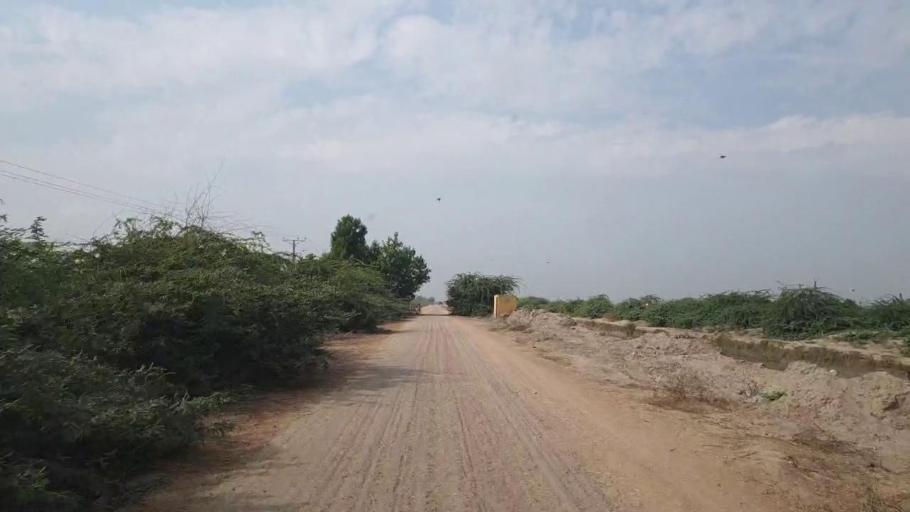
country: PK
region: Sindh
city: Kario
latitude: 24.6236
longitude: 68.5792
